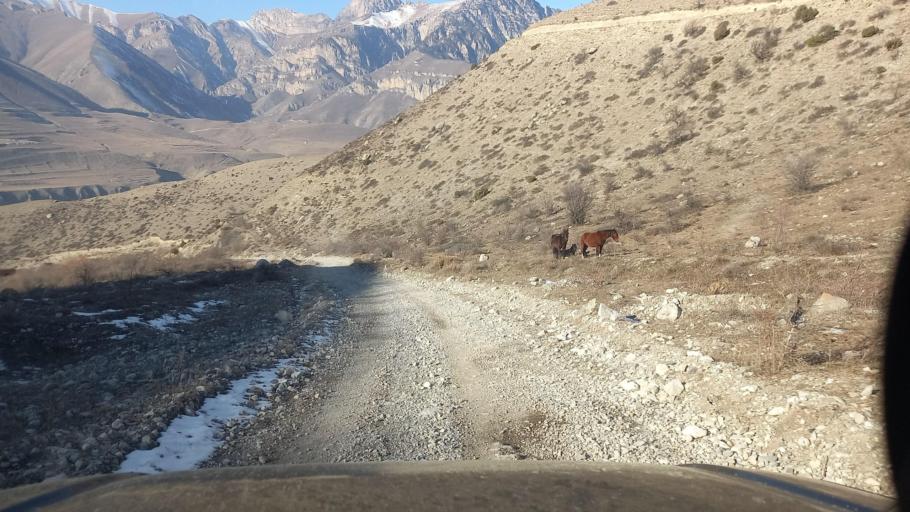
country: RU
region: Ingushetiya
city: Dzhayrakh
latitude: 42.8450
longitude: 44.6573
